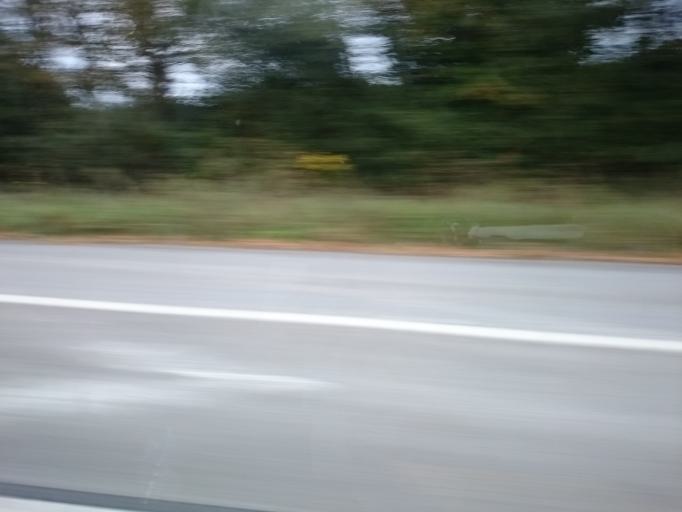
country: FR
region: Brittany
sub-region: Departement du Morbihan
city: Gestel
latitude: 47.8194
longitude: -3.4657
